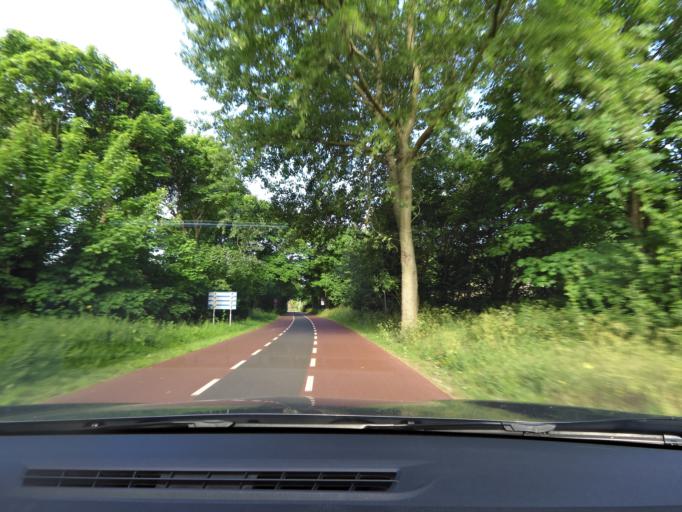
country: NL
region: Zeeland
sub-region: Schouwen-Duiveland
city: Renesse
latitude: 51.7419
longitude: 3.7866
